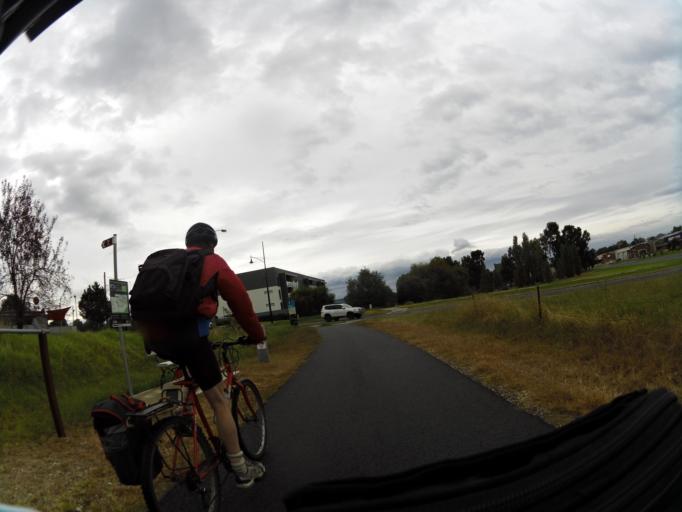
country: AU
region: Victoria
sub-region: Wodonga
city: Wodonga
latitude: -36.1231
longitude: 146.8931
